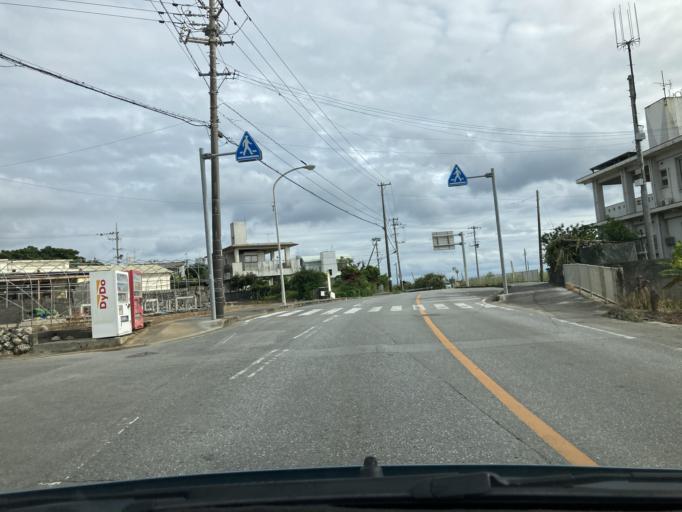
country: JP
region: Okinawa
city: Itoman
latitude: 26.1172
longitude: 127.6952
